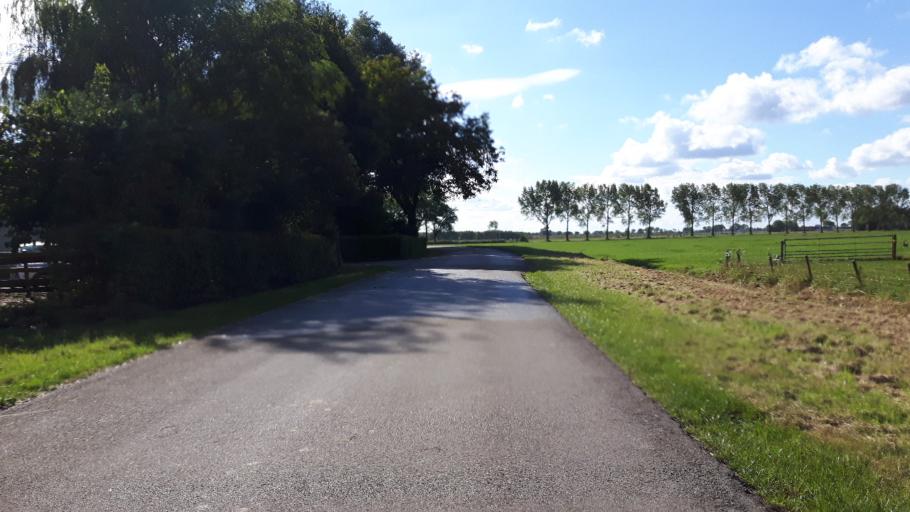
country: NL
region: Gelderland
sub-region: Gemeente Geldermalsen
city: Geldermalsen
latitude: 51.9252
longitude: 5.2857
